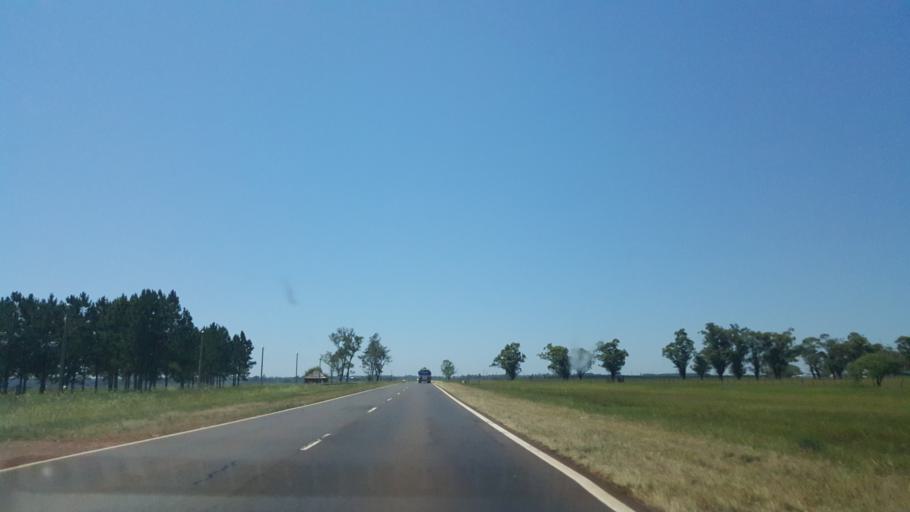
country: AR
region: Corrientes
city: Santo Tome
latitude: -28.5203
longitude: -56.1059
